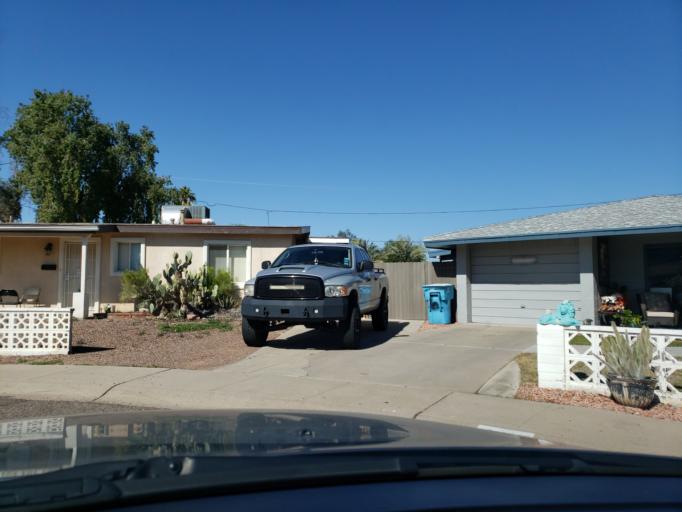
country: US
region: Arizona
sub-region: Maricopa County
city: Paradise Valley
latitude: 33.5991
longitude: -112.0339
